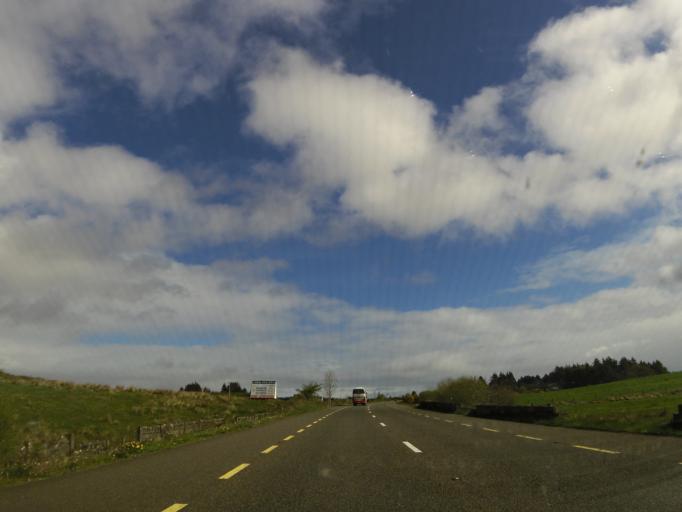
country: IE
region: Connaught
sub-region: Maigh Eo
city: Ballyhaunis
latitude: 53.8987
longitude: -8.7992
